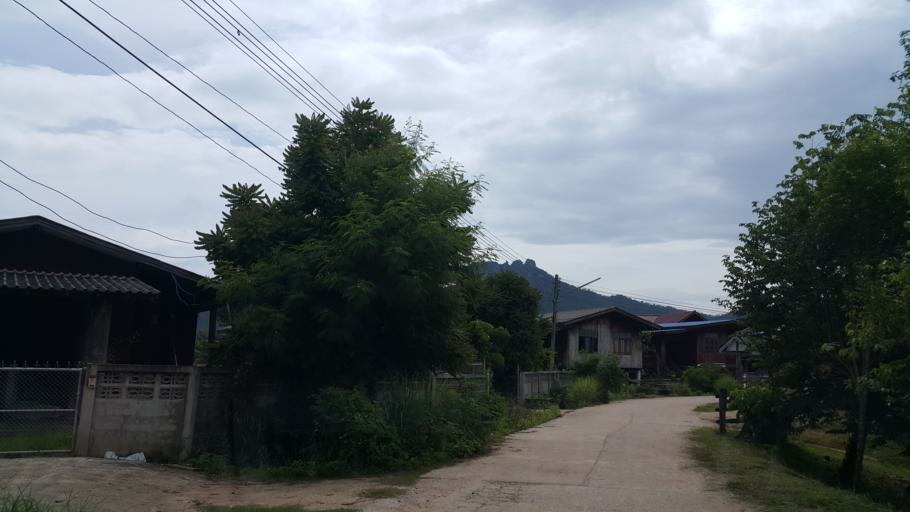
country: TH
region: Lampang
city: Chae Hom
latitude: 18.7449
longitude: 99.5656
